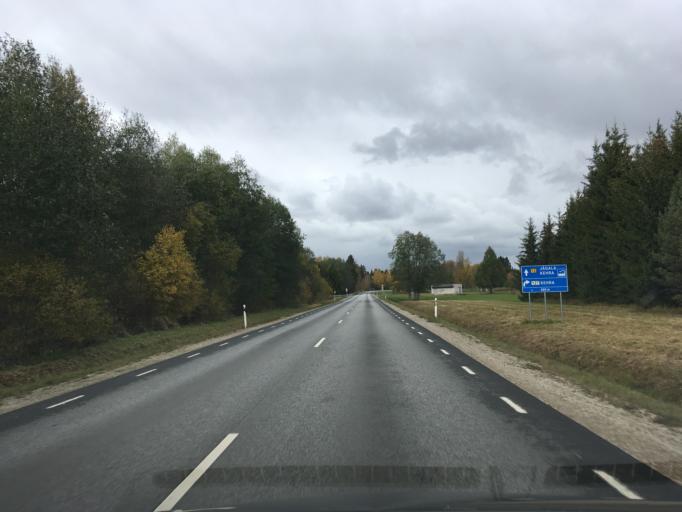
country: EE
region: Harju
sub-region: Anija vald
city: Kehra
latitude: 59.3093
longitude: 25.3501
